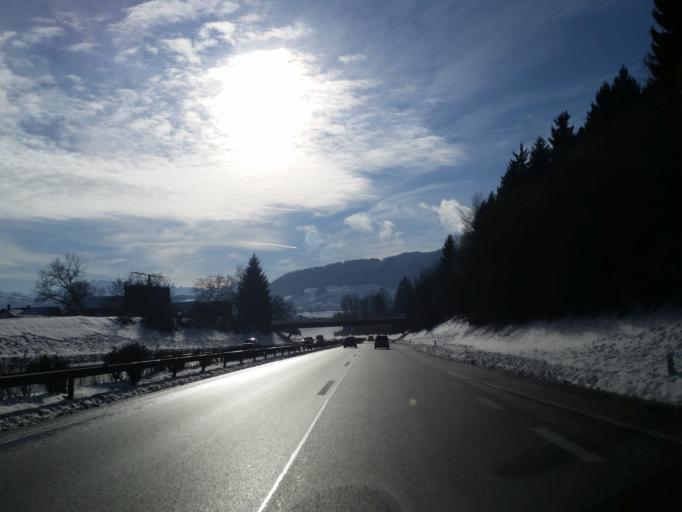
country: CH
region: Zurich
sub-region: Bezirk Horgen
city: Waedenswil / Eichweid
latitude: 47.2102
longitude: 8.6737
